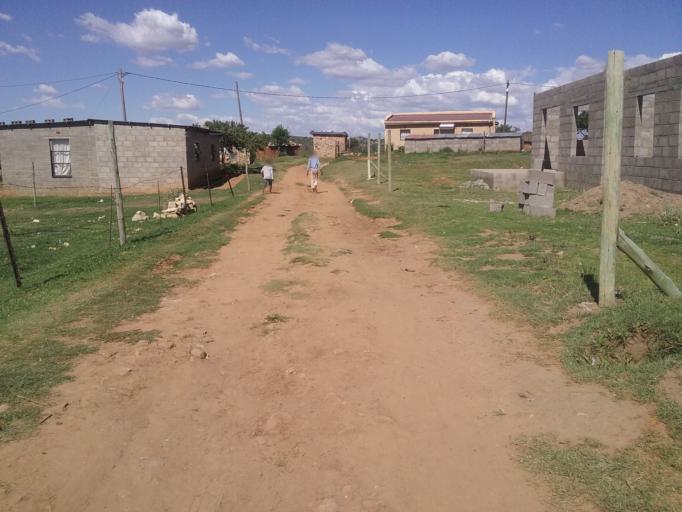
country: LS
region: Maseru
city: Maseru
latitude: -29.4157
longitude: 27.5660
